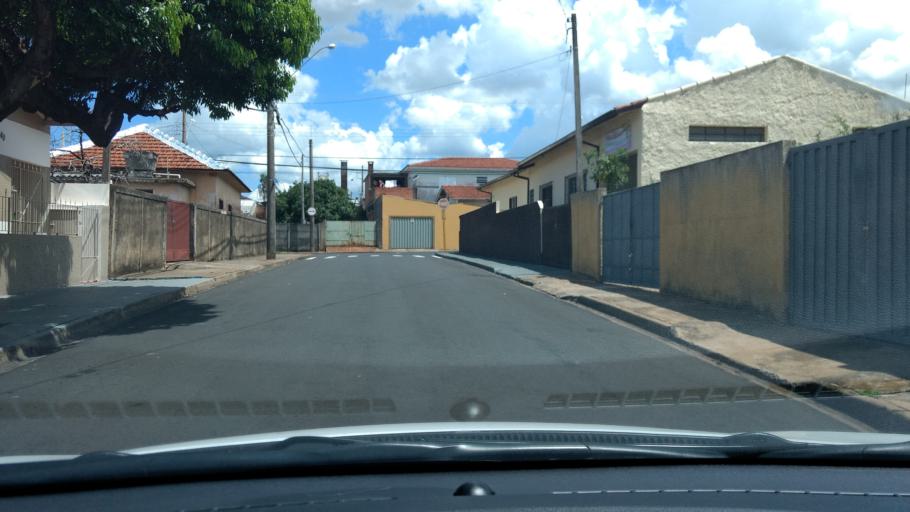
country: BR
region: Sao Paulo
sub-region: Botucatu
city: Botucatu
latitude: -22.8653
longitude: -48.4522
